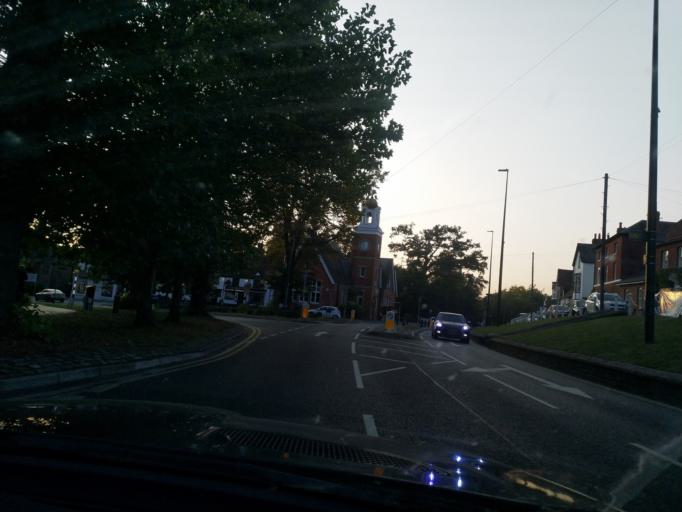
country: GB
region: England
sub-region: Kent
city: Sheerness
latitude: 51.4122
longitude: 0.8379
